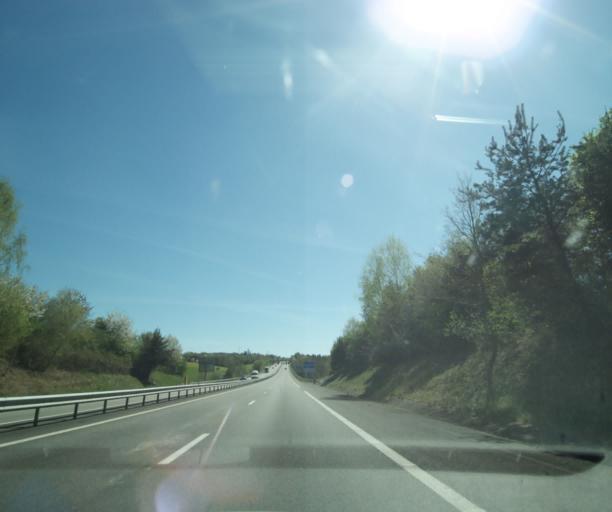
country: FR
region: Limousin
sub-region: Departement de la Haute-Vienne
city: Saint-Germain-les-Belles
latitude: 45.5487
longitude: 1.5082
